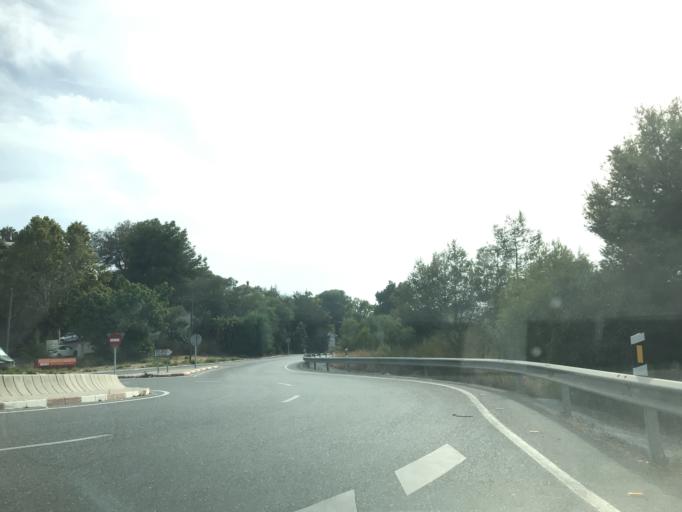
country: ES
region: Andalusia
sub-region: Provincia de Granada
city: Almunecar
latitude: 36.7370
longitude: -3.6788
